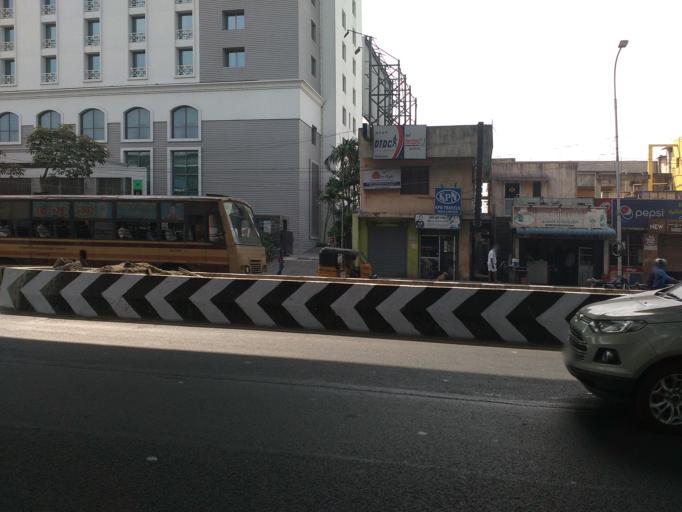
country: IN
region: Tamil Nadu
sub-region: Kancheepuram
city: Alandur
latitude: 13.0080
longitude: 80.2078
